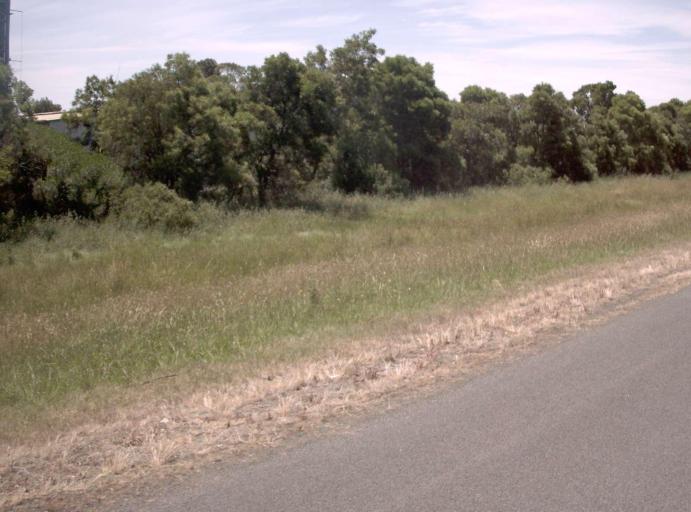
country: AU
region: Victoria
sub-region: Latrobe
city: Morwell
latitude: -38.2425
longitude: 146.4437
